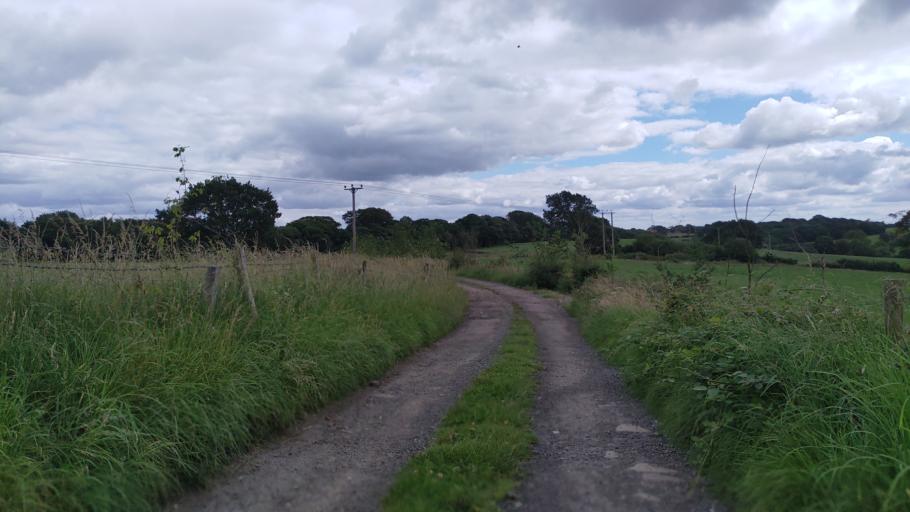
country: GB
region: England
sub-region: Lancashire
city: Coppull
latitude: 53.6273
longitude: -2.6383
